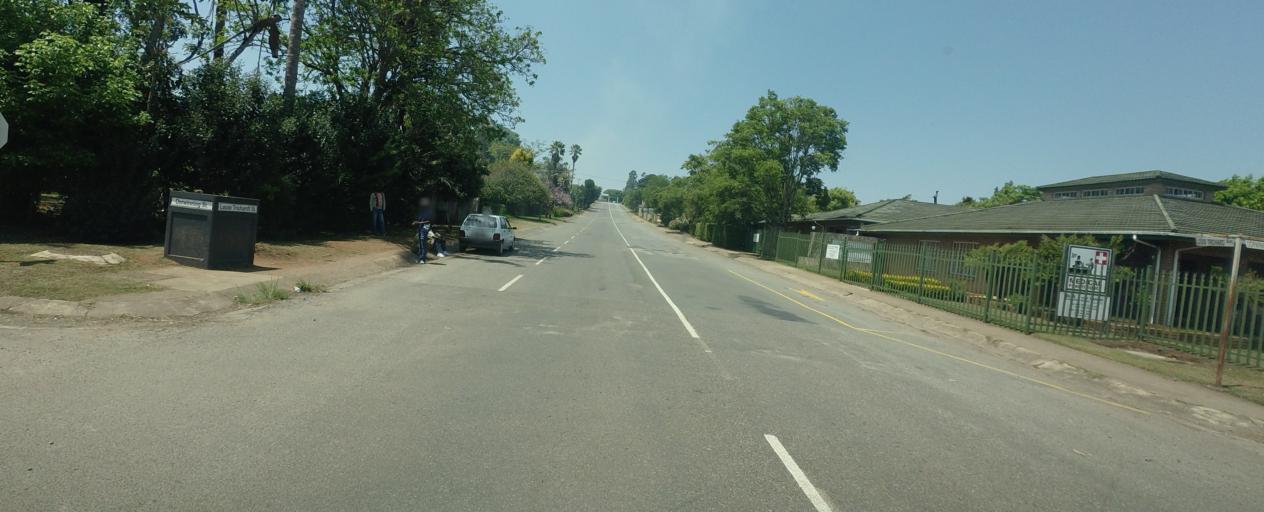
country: ZA
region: Mpumalanga
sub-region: Ehlanzeni District
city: Graksop
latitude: -24.9318
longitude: 30.8429
